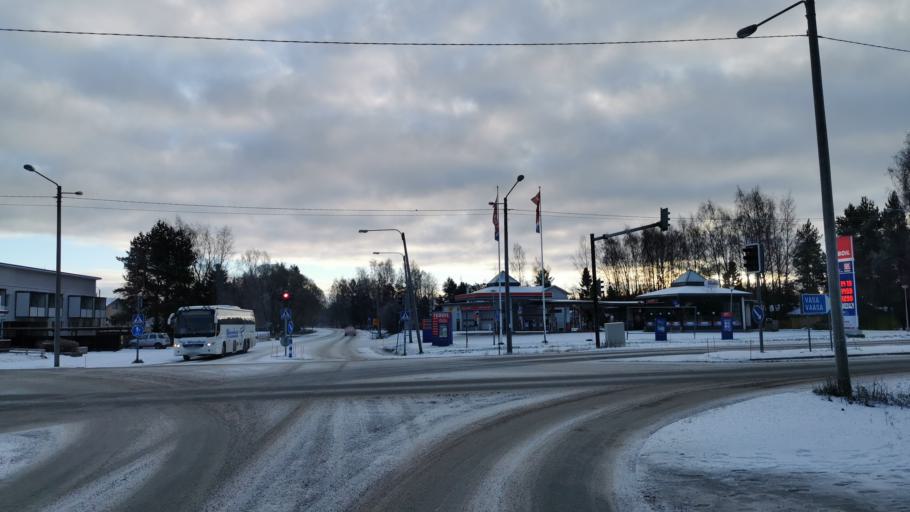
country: FI
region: Ostrobothnia
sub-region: Vaasa
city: Korsholm
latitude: 63.1152
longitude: 21.6856
